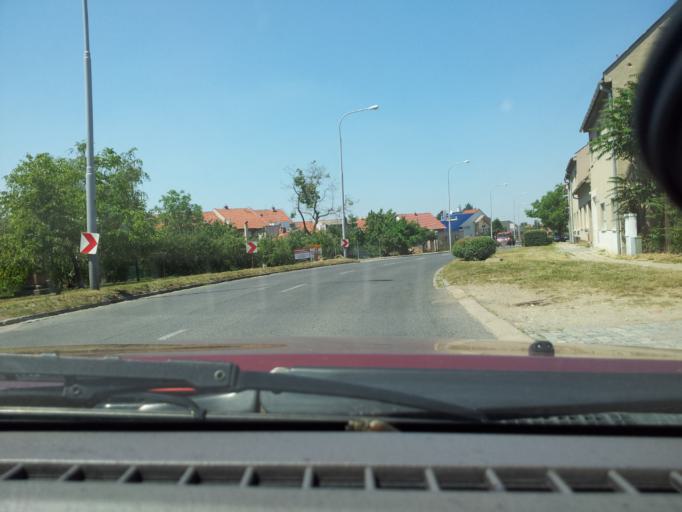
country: CZ
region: South Moravian
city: Sokolnice
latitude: 49.1418
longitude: 16.6670
